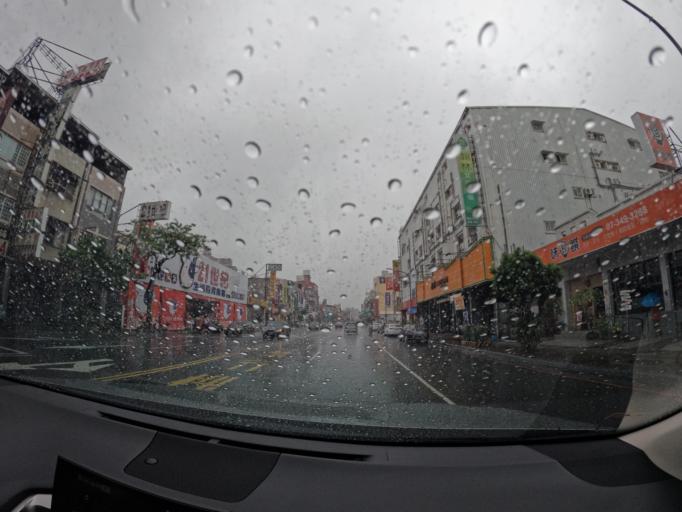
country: TW
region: Kaohsiung
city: Kaohsiung
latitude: 22.6673
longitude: 120.3215
